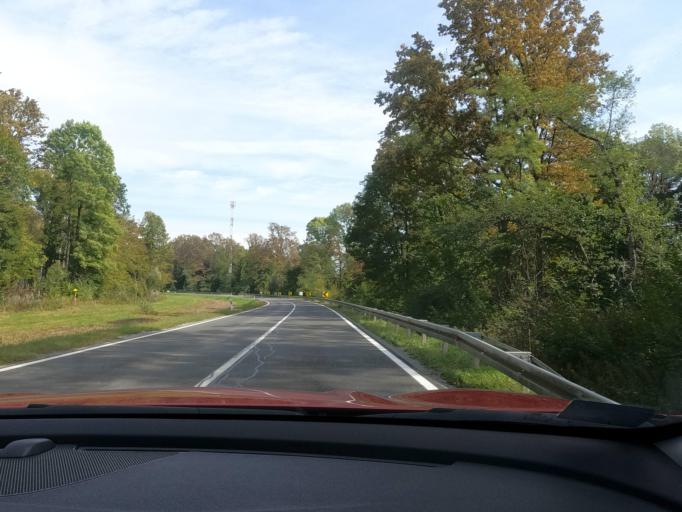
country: HR
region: Sisacko-Moslavacka
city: Budasevo
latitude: 45.4938
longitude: 16.5071
